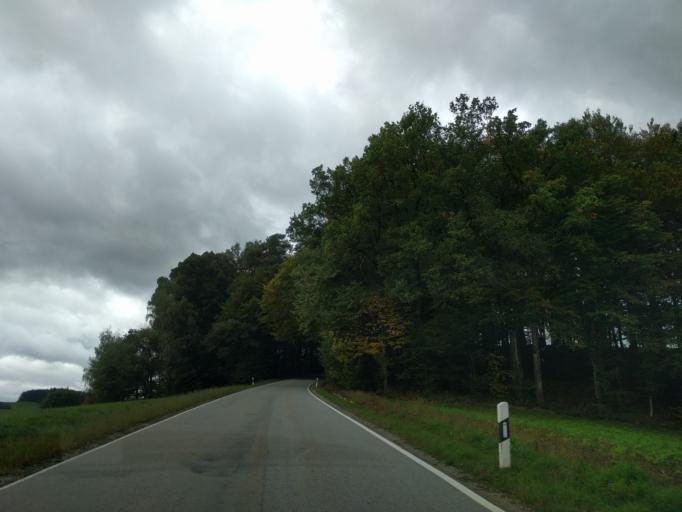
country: DE
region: Bavaria
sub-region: Lower Bavaria
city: Auerbach
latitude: 48.8143
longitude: 13.0806
